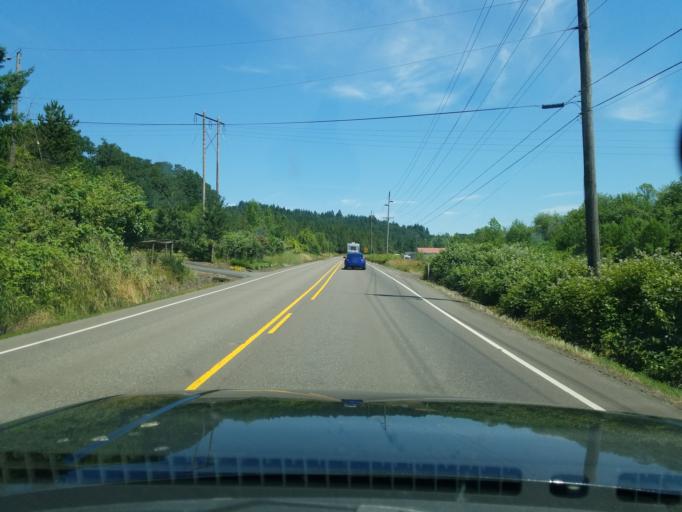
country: US
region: Oregon
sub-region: Yamhill County
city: Yamhill
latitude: 45.3701
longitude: -123.1613
